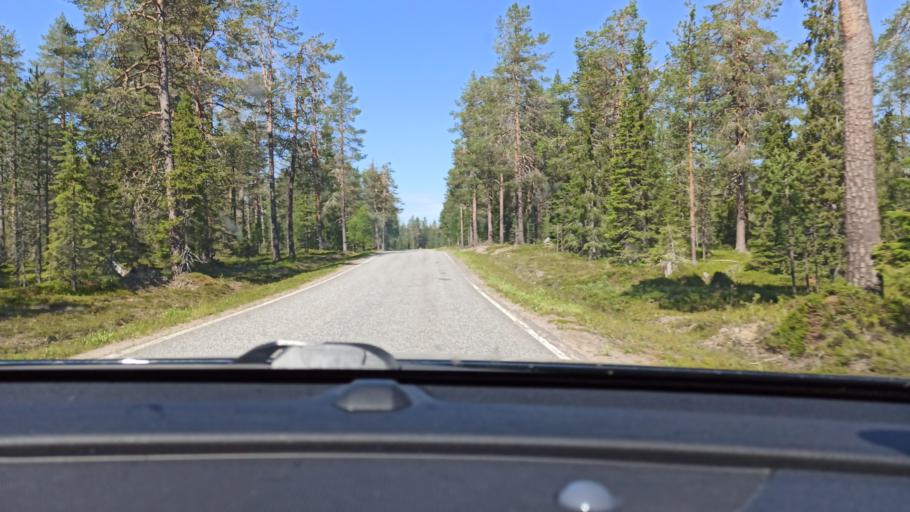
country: FI
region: Lapland
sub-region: Tunturi-Lappi
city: Kolari
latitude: 67.6693
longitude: 24.1568
